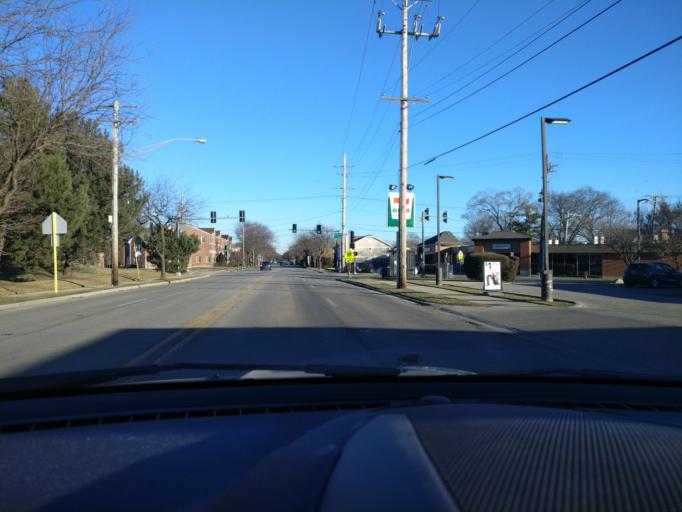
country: US
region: Illinois
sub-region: Cook County
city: Skokie
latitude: 42.0481
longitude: -87.7150
